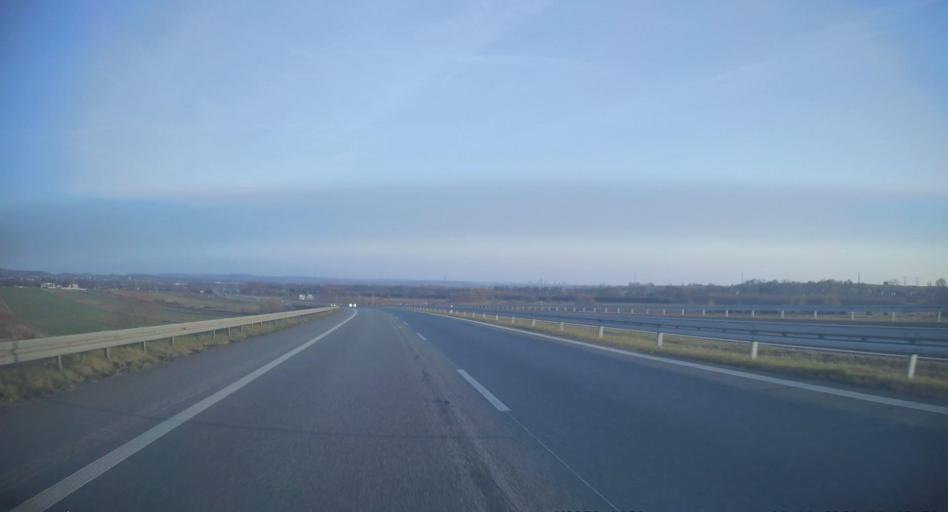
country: PL
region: Silesian Voivodeship
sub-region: Powiat bedzinski
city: Mierzecice
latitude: 50.4270
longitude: 19.1595
